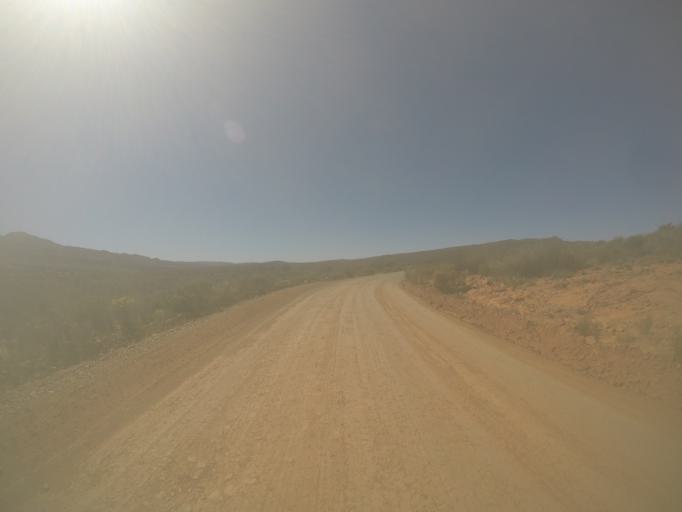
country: ZA
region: Western Cape
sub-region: West Coast District Municipality
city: Clanwilliam
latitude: -32.5010
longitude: 19.2789
